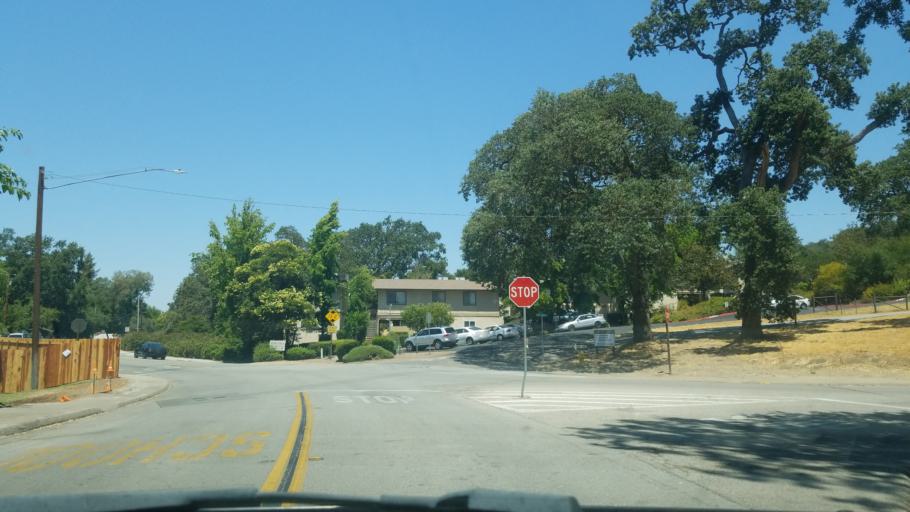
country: US
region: California
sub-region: San Luis Obispo County
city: Atascadero
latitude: 35.4931
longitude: -120.6650
